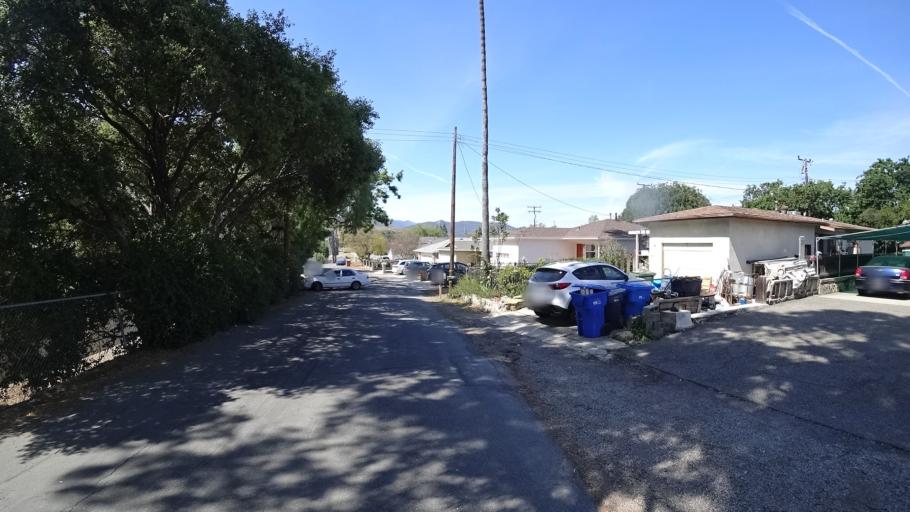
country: US
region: California
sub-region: Ventura County
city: Thousand Oaks
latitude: 34.1804
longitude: -118.8661
